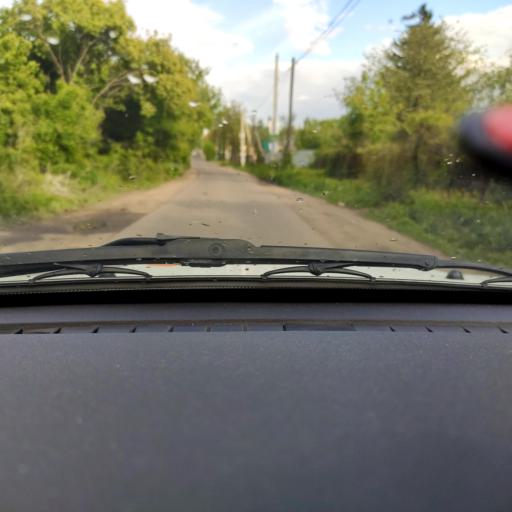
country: RU
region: Voronezj
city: Maslovka
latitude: 51.5843
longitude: 39.1607
